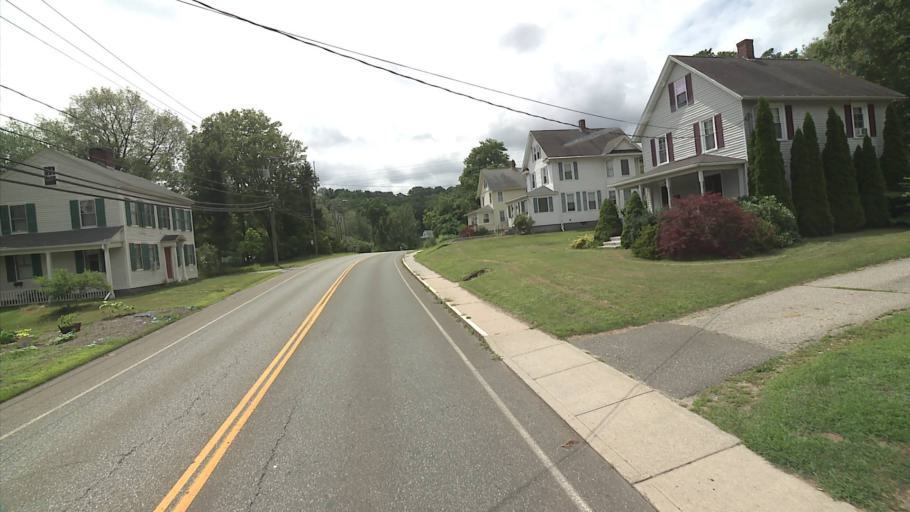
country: US
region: Connecticut
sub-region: Middlesex County
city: Deep River Center
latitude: 41.3820
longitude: -72.4395
